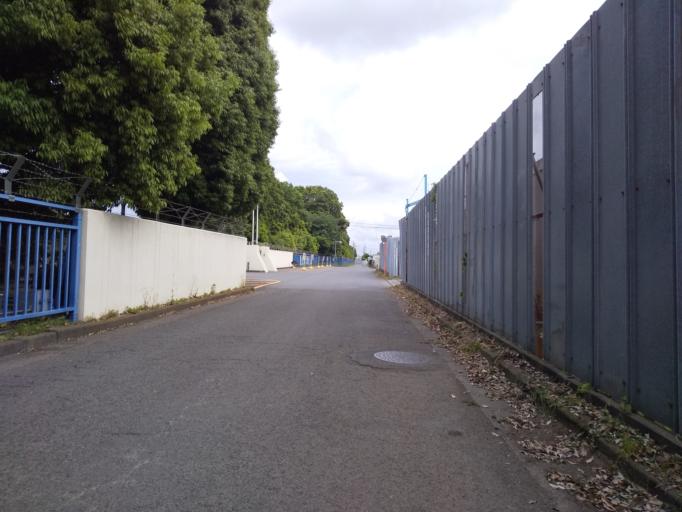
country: JP
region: Kanagawa
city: Zama
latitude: 35.5429
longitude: 139.3840
